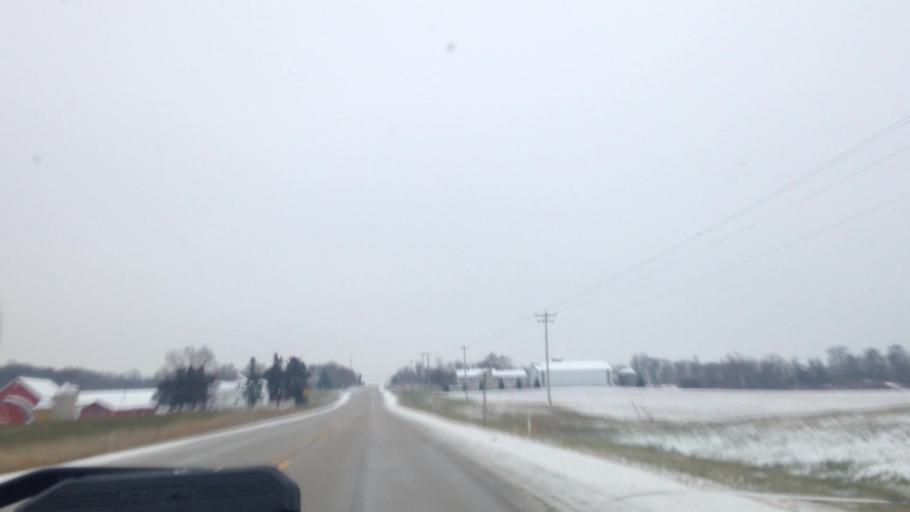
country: US
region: Wisconsin
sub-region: Dodge County
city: Hustisford
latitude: 43.2714
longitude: -88.5181
